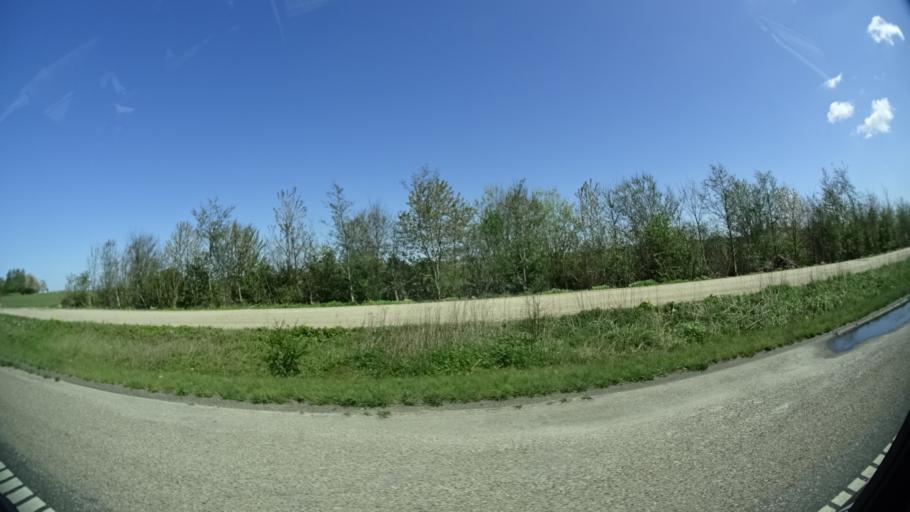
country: DK
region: Central Jutland
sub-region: Skanderborg Kommune
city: Horning
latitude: 56.1119
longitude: 10.0401
